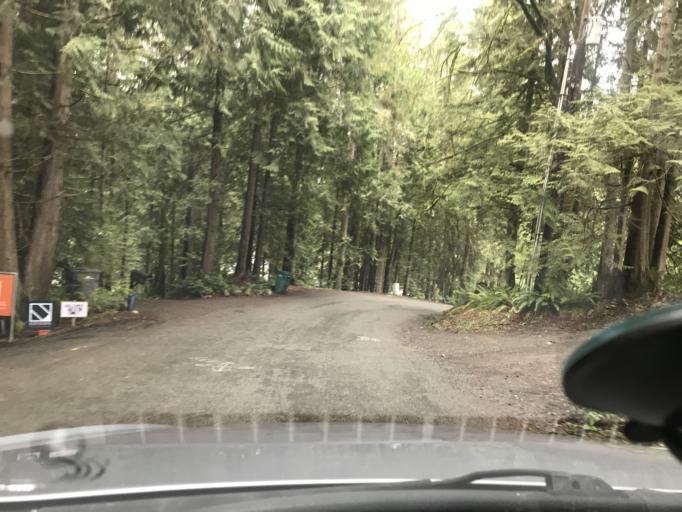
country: US
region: Washington
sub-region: King County
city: Ames Lake
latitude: 47.6369
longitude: -121.9577
